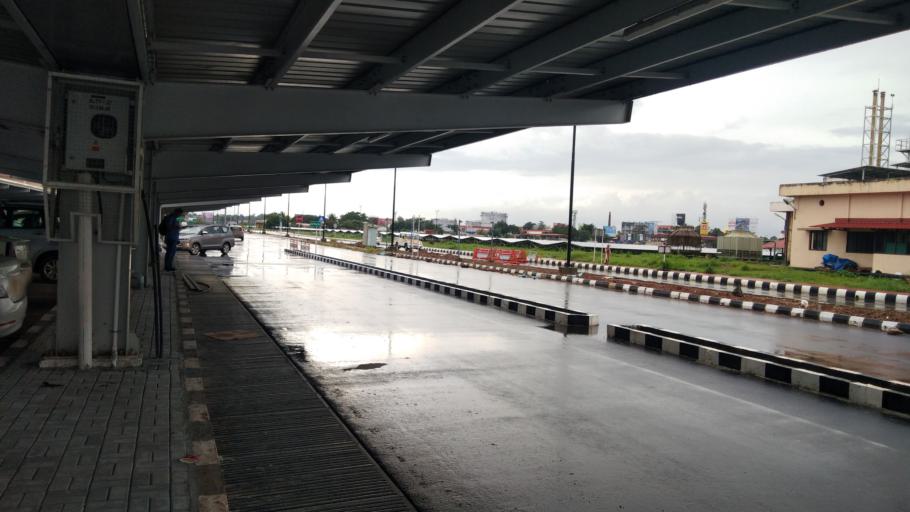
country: IN
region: Kerala
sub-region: Ernakulam
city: Angamali
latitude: 10.1571
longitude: 76.3895
